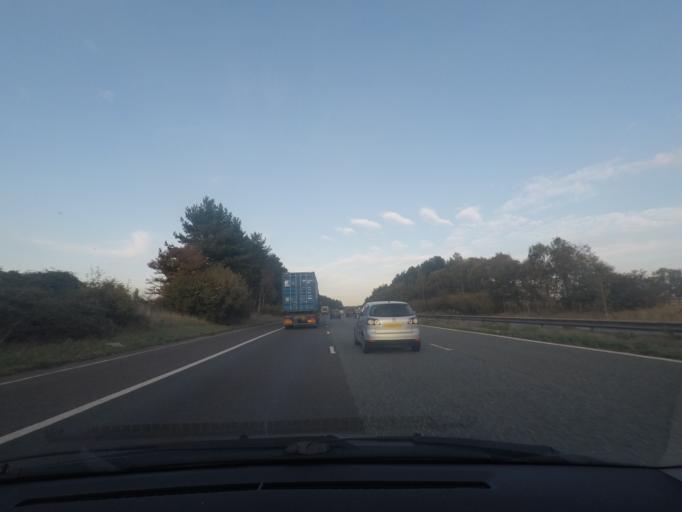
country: GB
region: England
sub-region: North Lincolnshire
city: Worlaby
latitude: 53.5718
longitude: -0.4711
